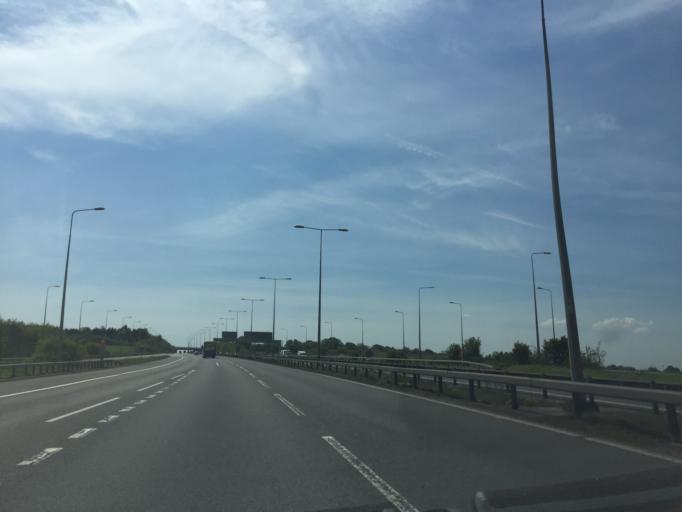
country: GB
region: England
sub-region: Essex
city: Epping
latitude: 51.6768
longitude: 0.1224
